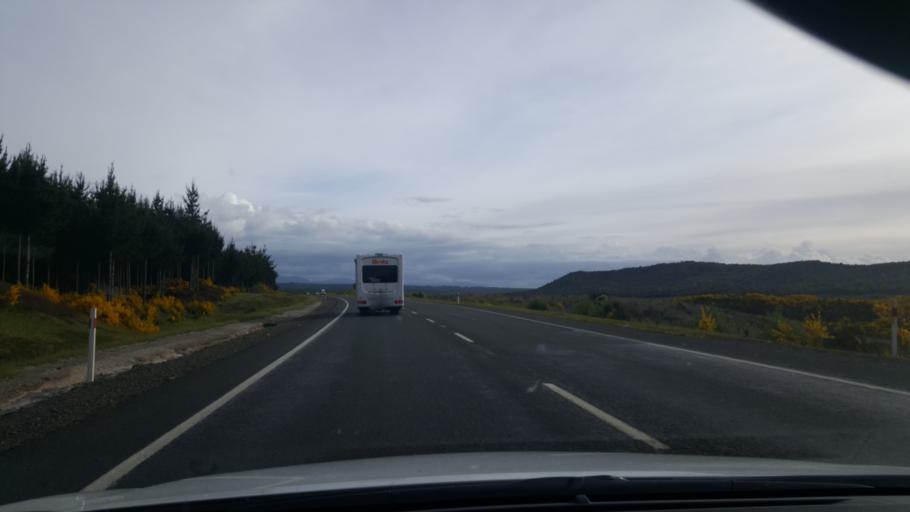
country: NZ
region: Waikato
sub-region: Taupo District
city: Taupo
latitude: -38.8292
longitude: 176.0664
